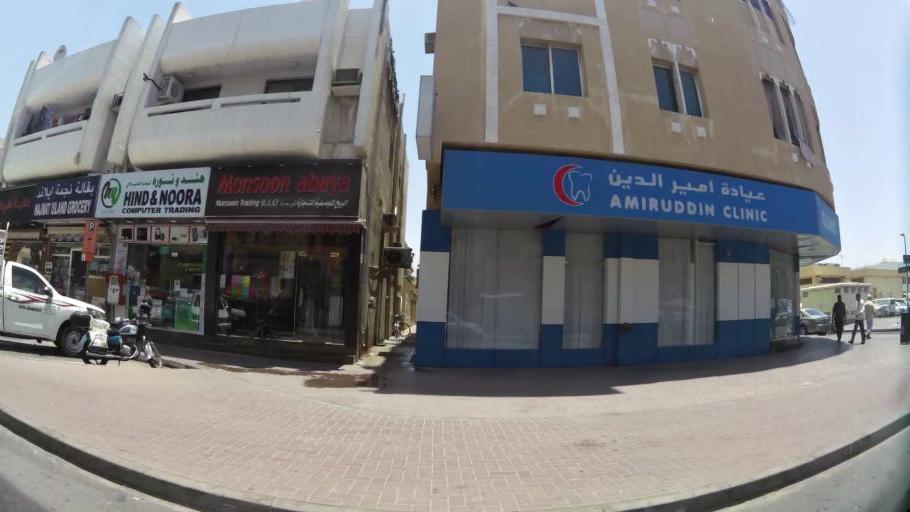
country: AE
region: Ash Shariqah
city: Sharjah
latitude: 25.2751
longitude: 55.3319
